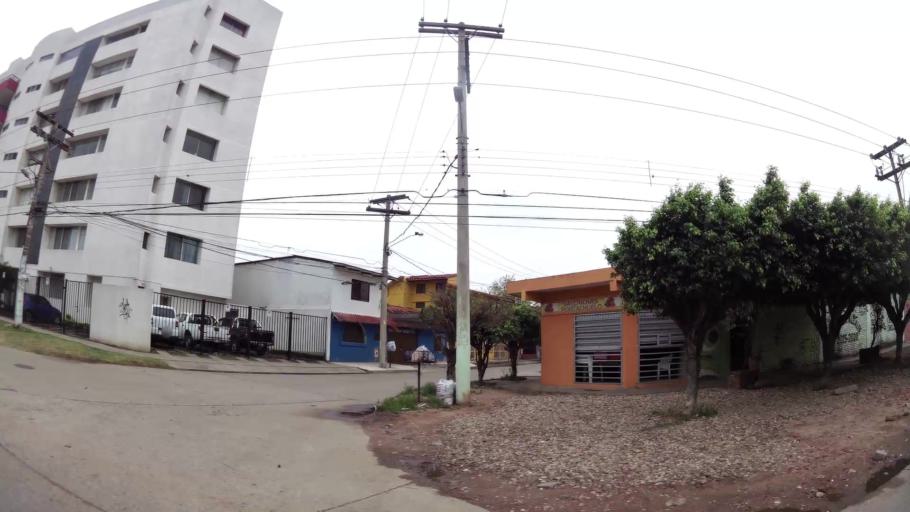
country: BO
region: Santa Cruz
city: Santa Cruz de la Sierra
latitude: -17.7580
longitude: -63.1810
